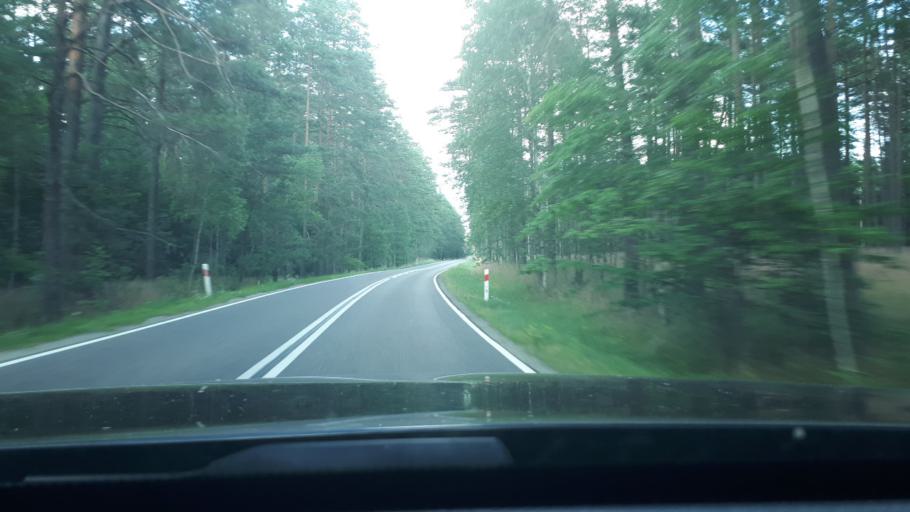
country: PL
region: Warmian-Masurian Voivodeship
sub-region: Powiat olsztynski
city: Stawiguda
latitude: 53.5374
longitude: 20.5223
